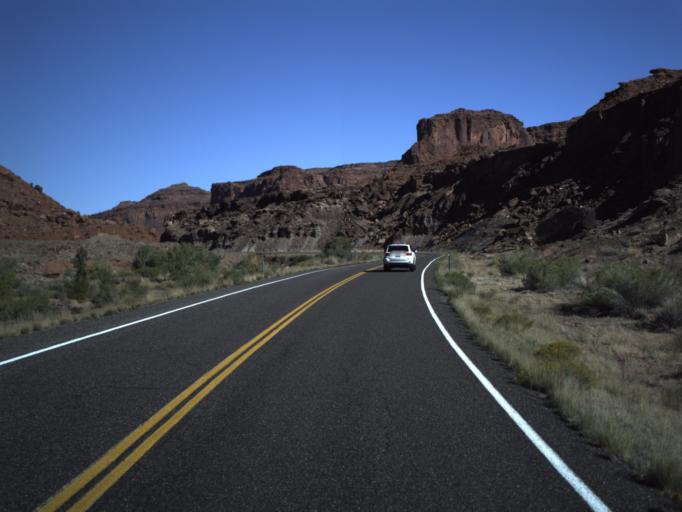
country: US
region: Utah
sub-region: San Juan County
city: Blanding
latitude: 37.9197
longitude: -110.4633
